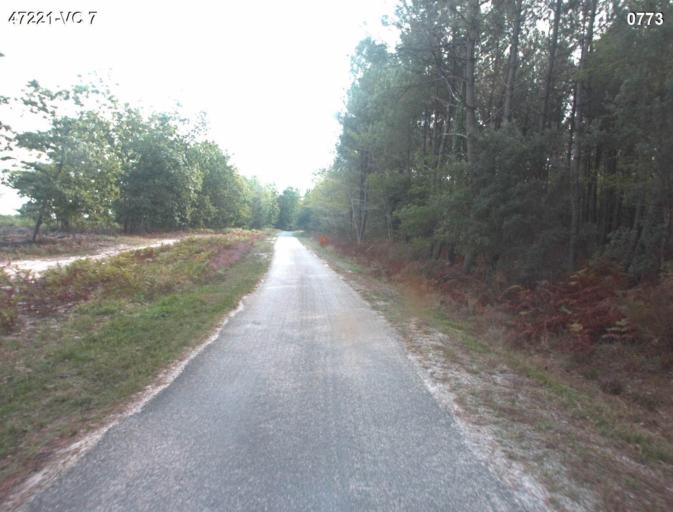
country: FR
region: Aquitaine
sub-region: Departement du Lot-et-Garonne
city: Mezin
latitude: 44.0930
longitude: 0.2235
